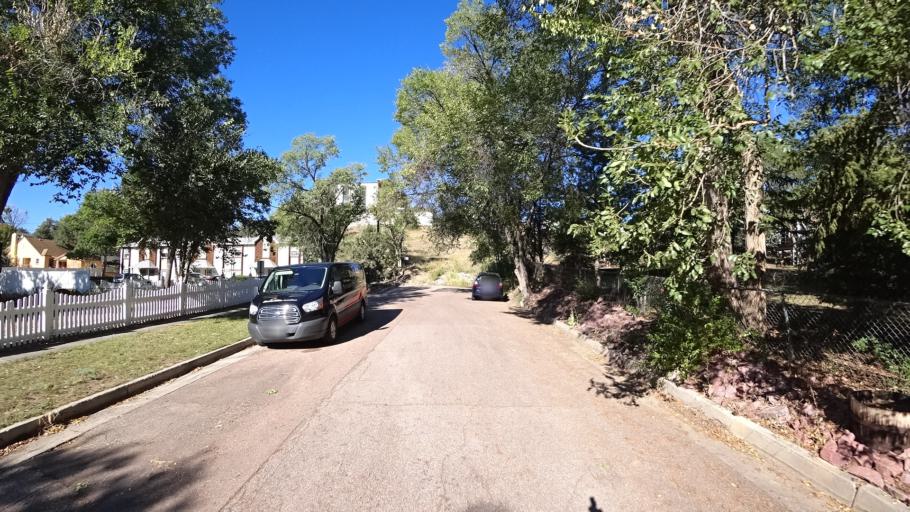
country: US
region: Colorado
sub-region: El Paso County
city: Colorado Springs
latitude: 38.8444
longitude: -104.8353
